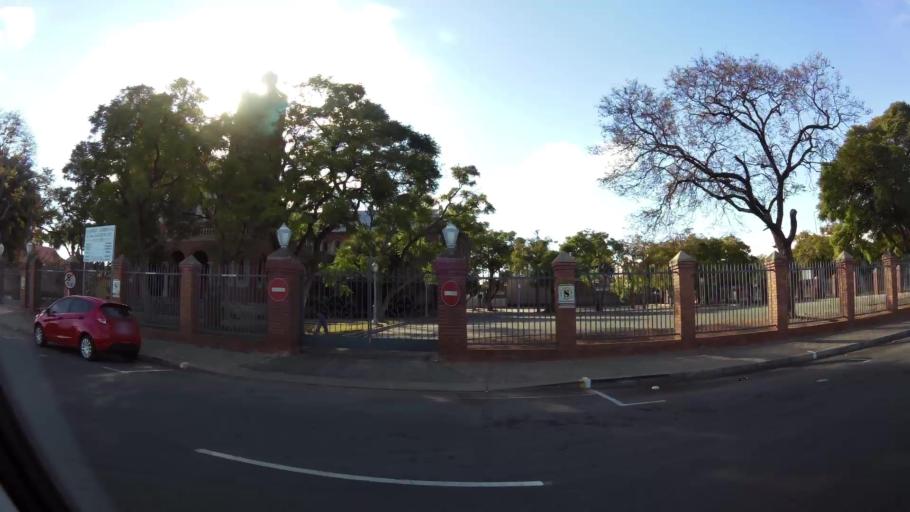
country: ZA
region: Limpopo
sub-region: Capricorn District Municipality
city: Polokwane
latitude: -23.9102
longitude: 29.4567
